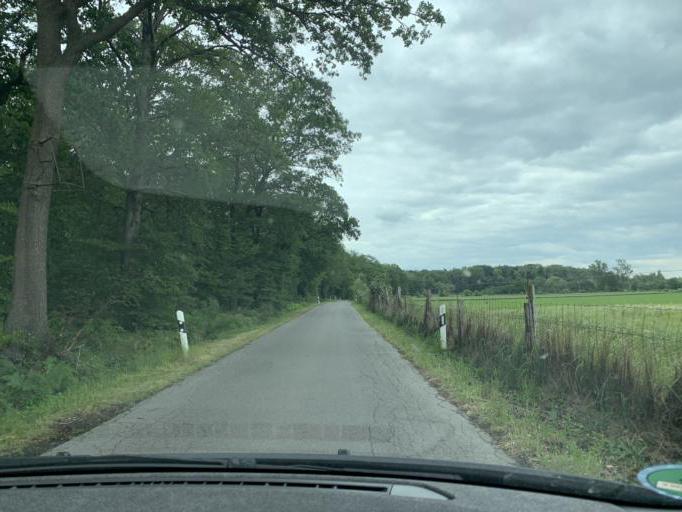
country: DE
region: North Rhine-Westphalia
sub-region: Regierungsbezirk Koln
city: Niederzier
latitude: 50.8781
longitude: 6.5124
